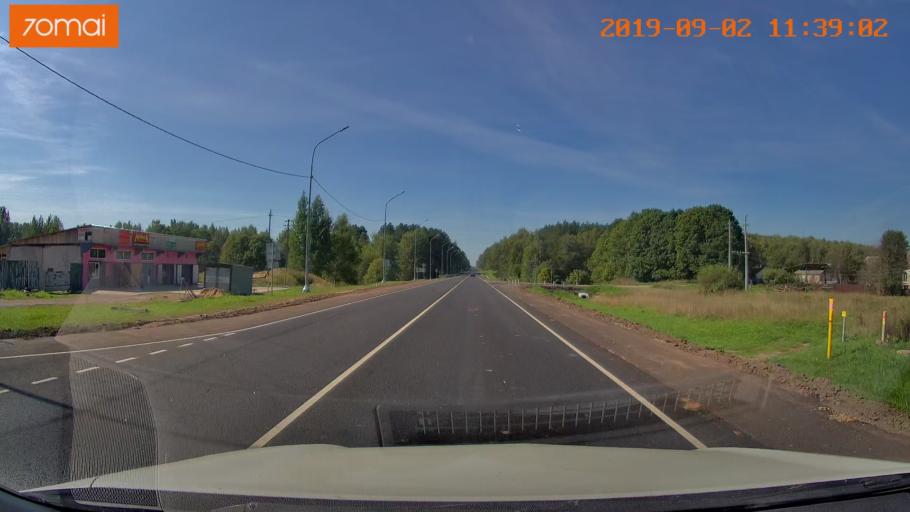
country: RU
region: Smolensk
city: Oster
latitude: 53.9102
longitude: 32.7303
